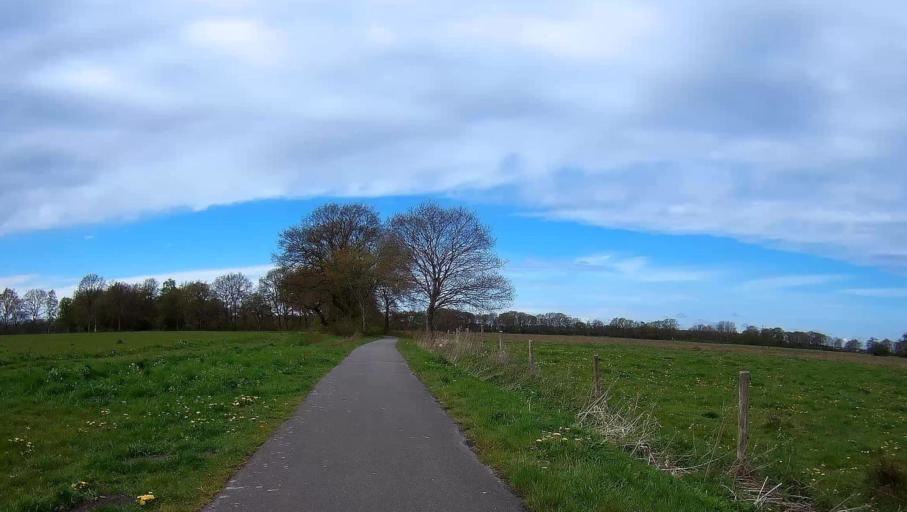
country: NL
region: Drenthe
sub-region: Gemeente Aa en Hunze
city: Anloo
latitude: 52.9644
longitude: 6.7105
